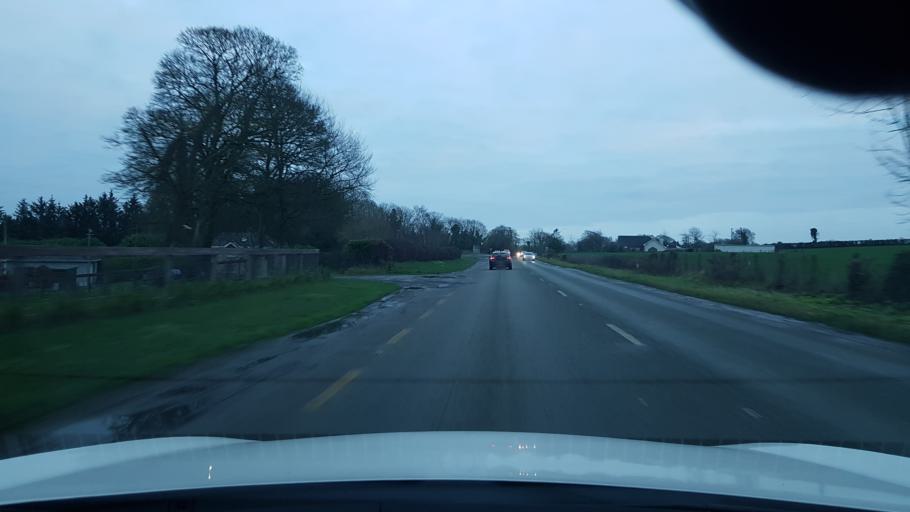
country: IE
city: Kentstown
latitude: 53.5910
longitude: -6.5998
